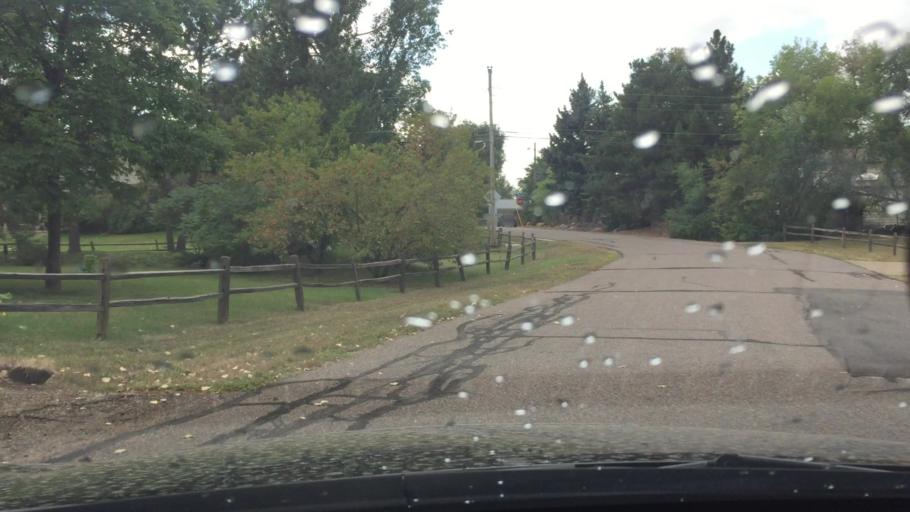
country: US
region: Colorado
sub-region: Jefferson County
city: Lakewood
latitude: 39.6799
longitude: -105.1133
